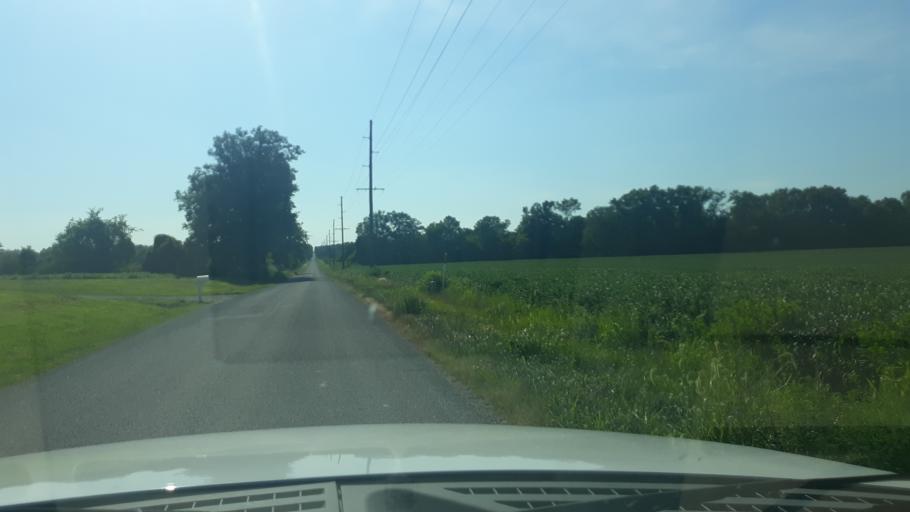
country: US
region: Illinois
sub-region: Saline County
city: Eldorado
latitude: 37.8630
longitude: -88.5111
